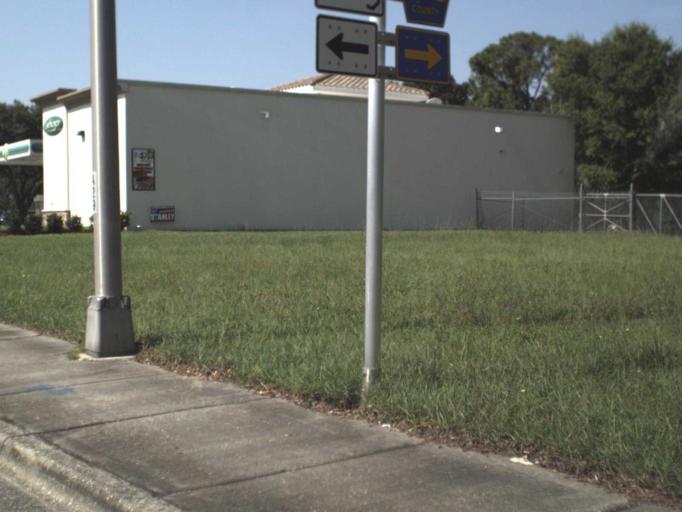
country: US
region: Florida
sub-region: Hillsborough County
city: Lake Magdalene
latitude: 28.0890
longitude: -82.4597
